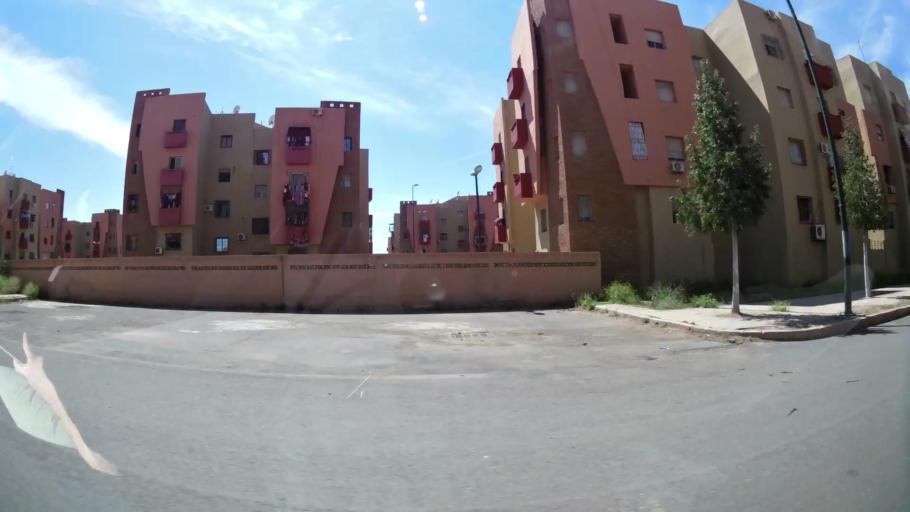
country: MA
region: Marrakech-Tensift-Al Haouz
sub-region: Marrakech
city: Marrakesh
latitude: 31.6358
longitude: -8.0778
